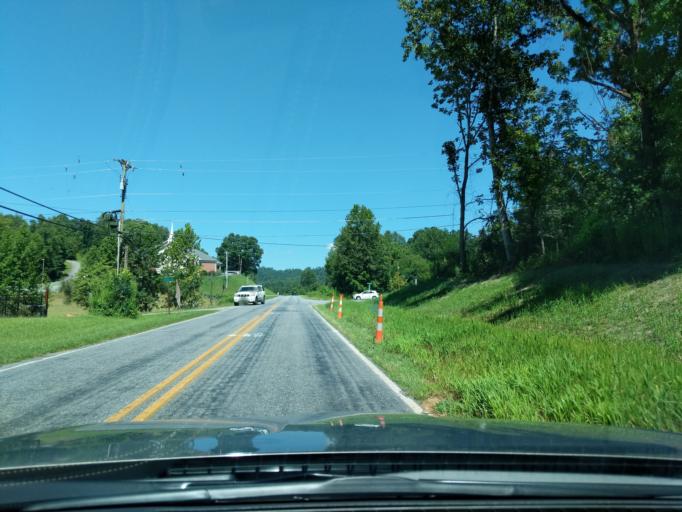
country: US
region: Georgia
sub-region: Towns County
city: Hiawassee
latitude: 35.0287
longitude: -83.7362
